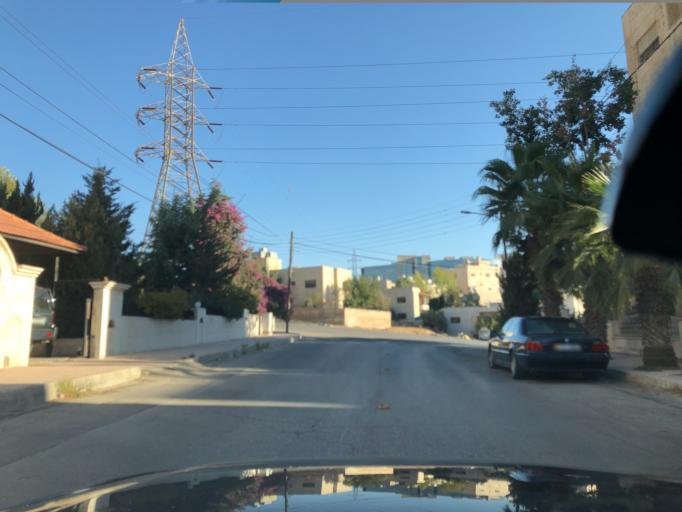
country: JO
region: Amman
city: Wadi as Sir
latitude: 31.9483
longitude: 35.8576
